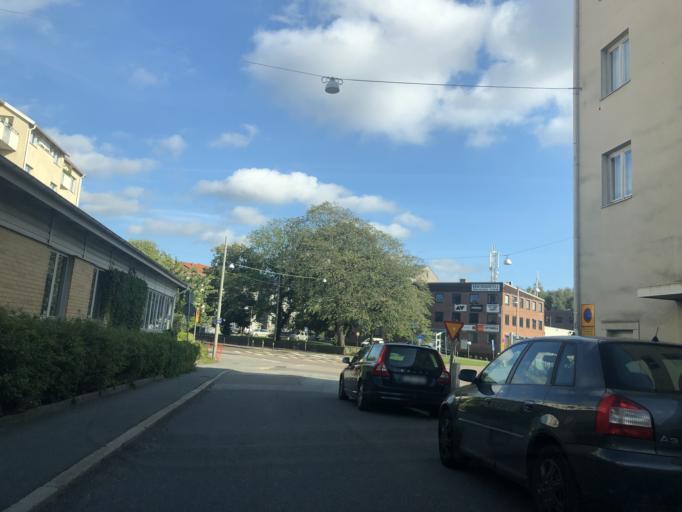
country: SE
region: Vaestra Goetaland
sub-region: Goteborg
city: Majorna
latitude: 57.6829
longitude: 11.9078
